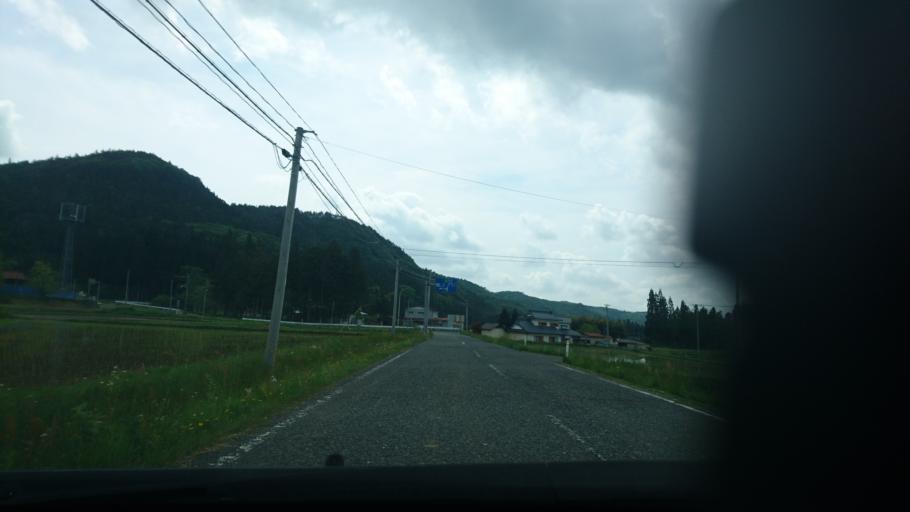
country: JP
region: Iwate
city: Ichinoseki
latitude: 38.8910
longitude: 140.9480
